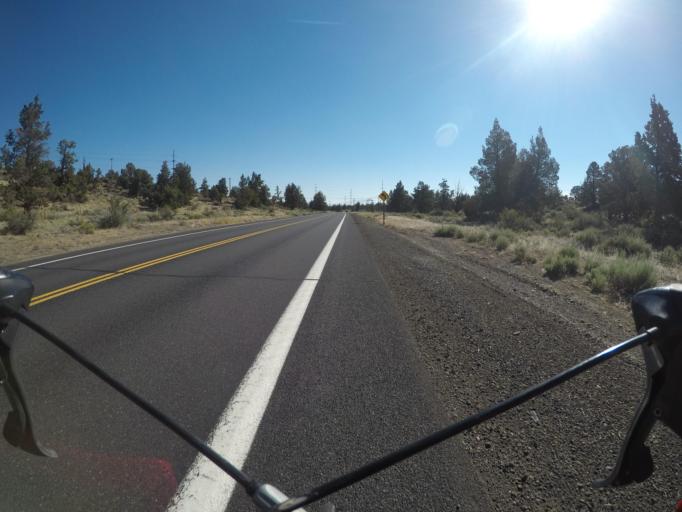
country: US
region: Oregon
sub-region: Deschutes County
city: Redmond
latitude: 44.2531
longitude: -121.2729
